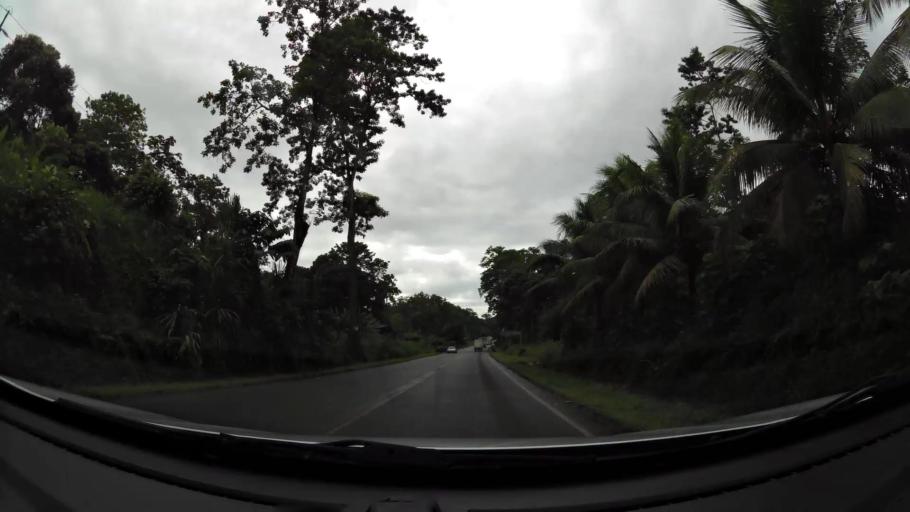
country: CR
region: Limon
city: Pocora
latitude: 10.1369
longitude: -83.5647
